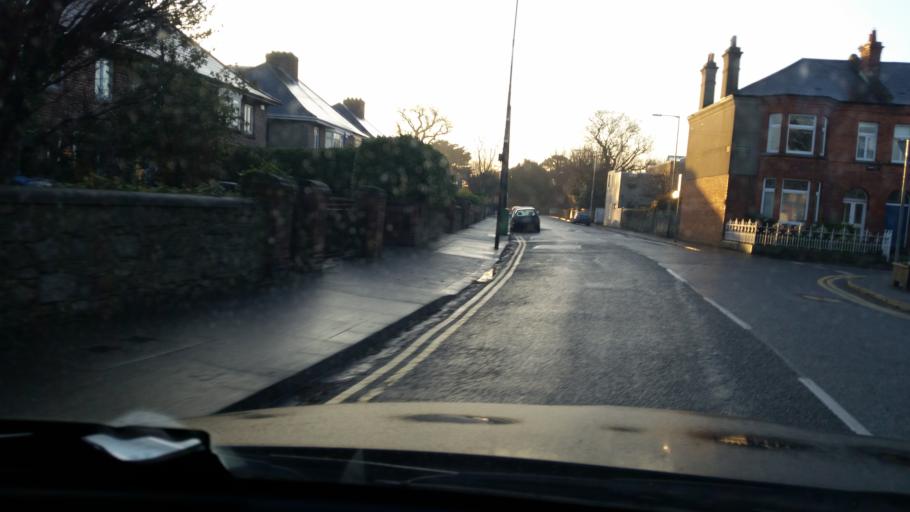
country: IE
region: Leinster
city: Sandymount
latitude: 53.3307
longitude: -6.2158
